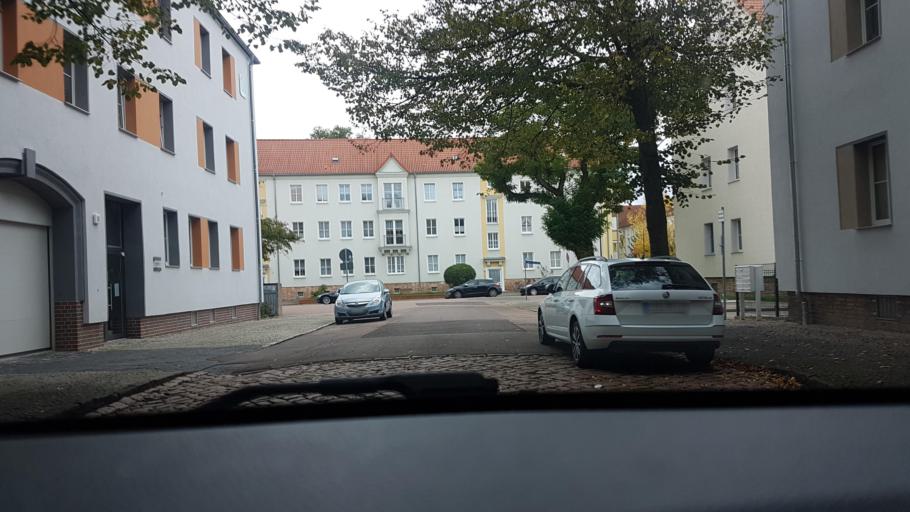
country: DE
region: Saxony-Anhalt
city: Bernburg
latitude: 51.7865
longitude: 11.7447
